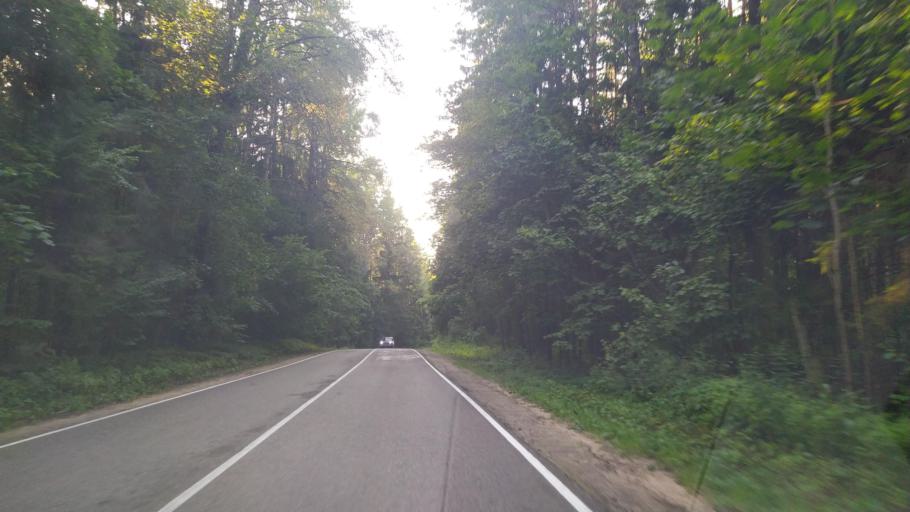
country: RU
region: Pskov
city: Pushkinskiye Gory
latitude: 57.0355
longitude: 28.9148
